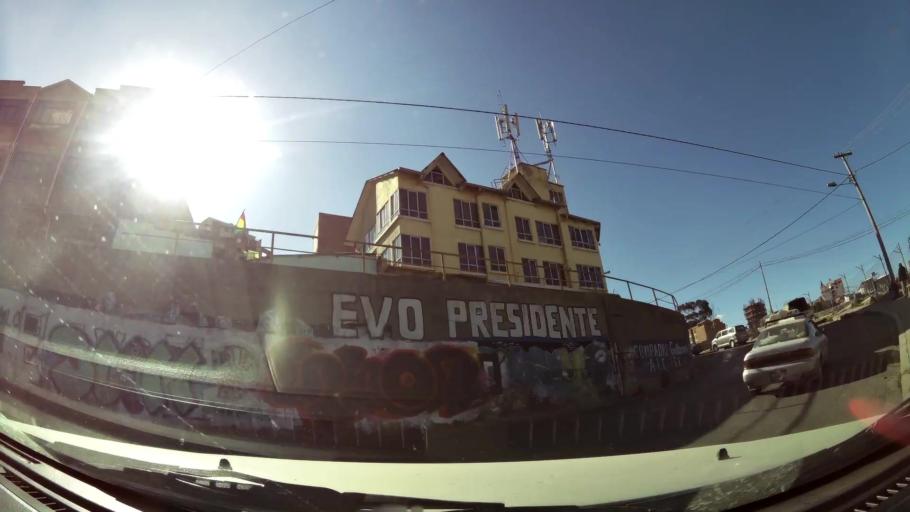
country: BO
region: La Paz
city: La Paz
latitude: -16.5195
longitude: -68.1275
